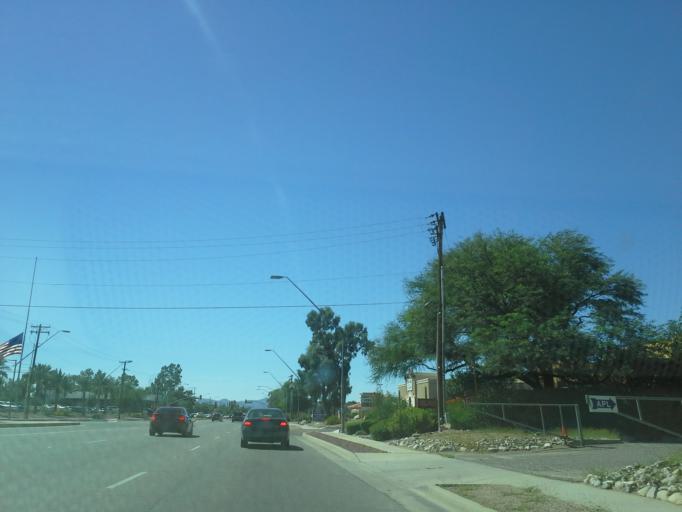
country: US
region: Arizona
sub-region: Pima County
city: Tucson
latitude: 32.2508
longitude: -110.8554
